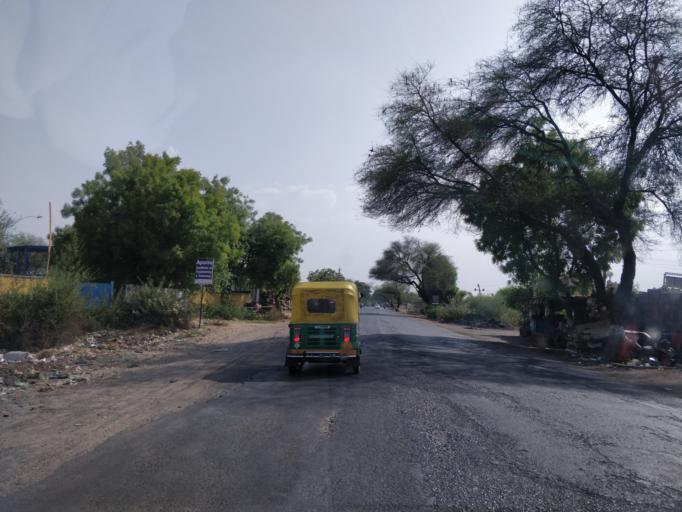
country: IN
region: Gujarat
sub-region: Ahmadabad
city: Naroda
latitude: 23.0992
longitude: 72.7026
